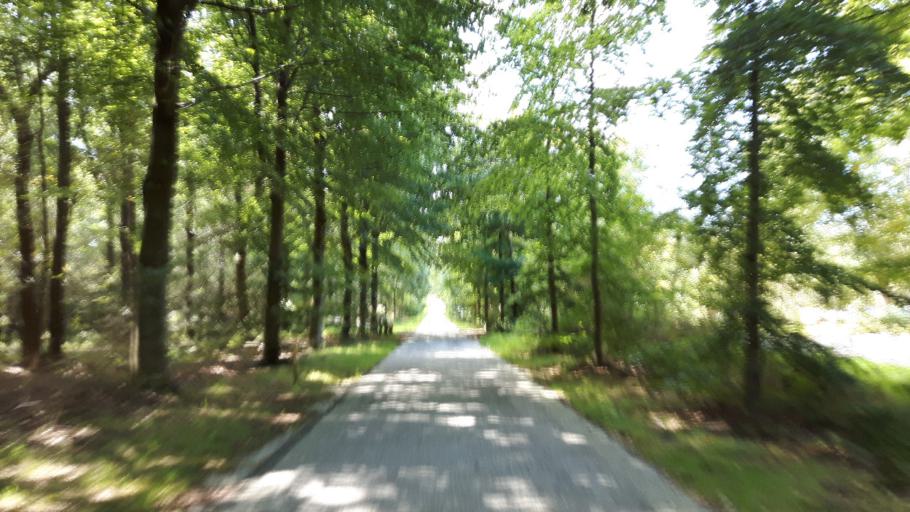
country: NL
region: Friesland
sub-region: Gemeente Smallingerland
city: Drachtstercompagnie
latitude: 53.0767
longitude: 6.2474
